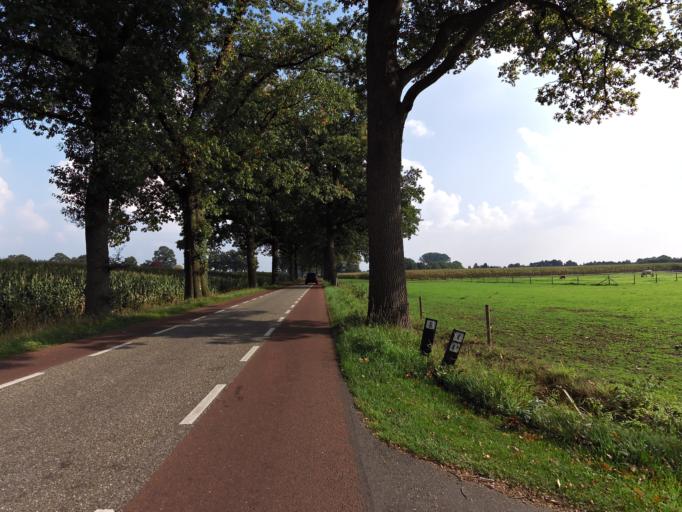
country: NL
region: Gelderland
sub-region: Oude IJsselstreek
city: Varsseveld
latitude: 51.9015
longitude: 6.4665
